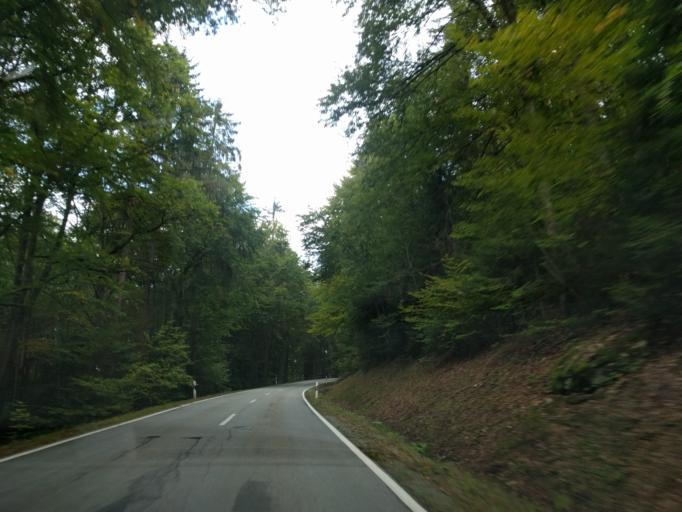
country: DE
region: Bavaria
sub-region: Lower Bavaria
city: Grafling
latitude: 48.8648
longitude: 12.9802
